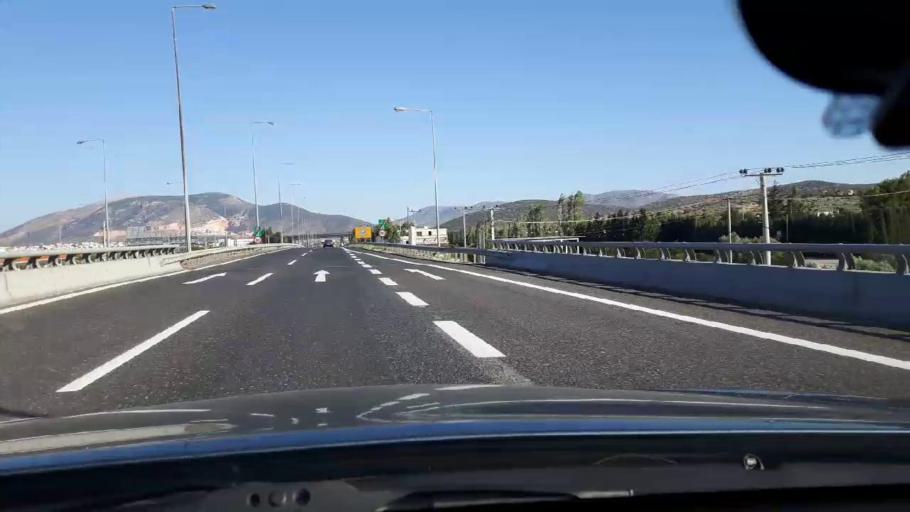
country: GR
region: Attica
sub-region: Nomarchia Anatolikis Attikis
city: Markopoulo
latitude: 37.8962
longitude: 23.9111
